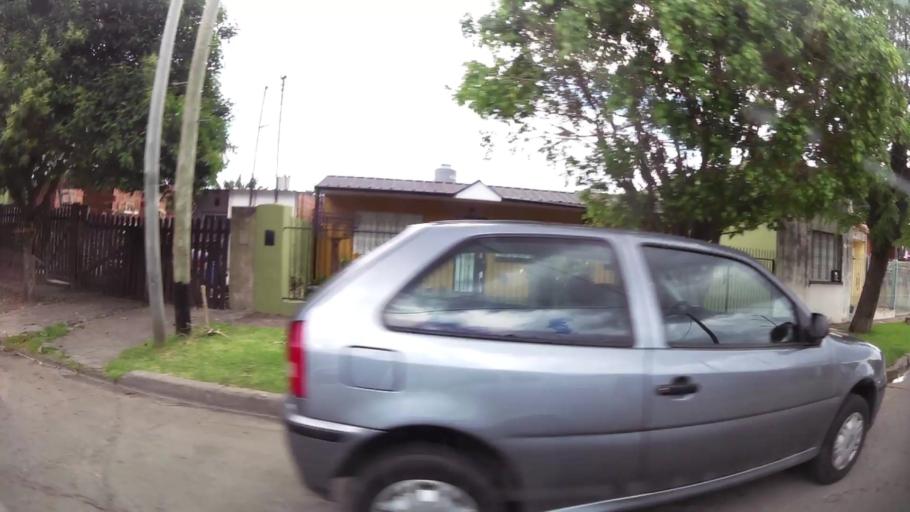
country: AR
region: Buenos Aires
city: Ituzaingo
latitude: -34.6381
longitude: -58.6877
